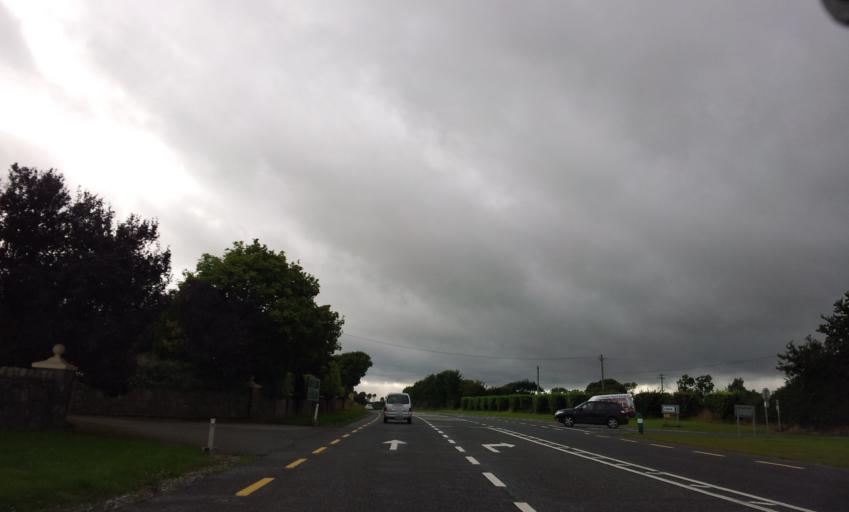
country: IE
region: Munster
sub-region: County Cork
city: Youghal
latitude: 51.9376
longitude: -7.9488
